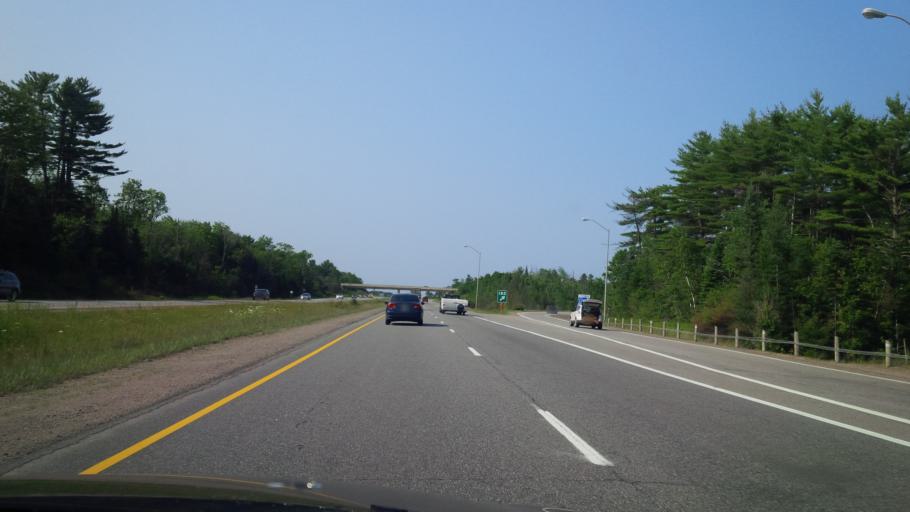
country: CA
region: Ontario
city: Bracebridge
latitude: 44.9997
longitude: -79.3039
